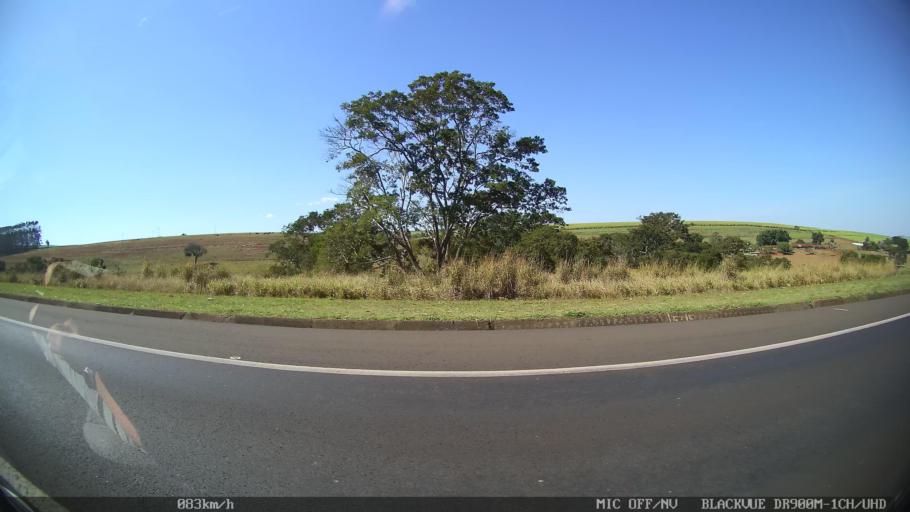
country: BR
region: Sao Paulo
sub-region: Franca
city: Franca
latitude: -20.6987
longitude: -47.5004
